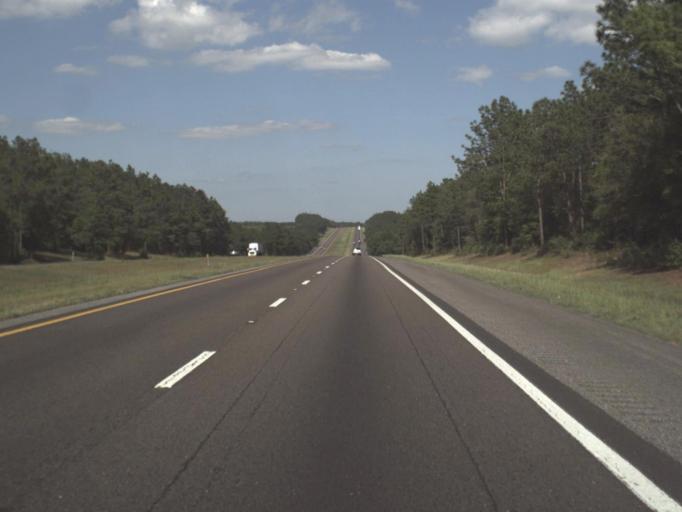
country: US
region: Florida
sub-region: Santa Rosa County
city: East Milton
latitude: 30.6602
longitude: -86.8692
